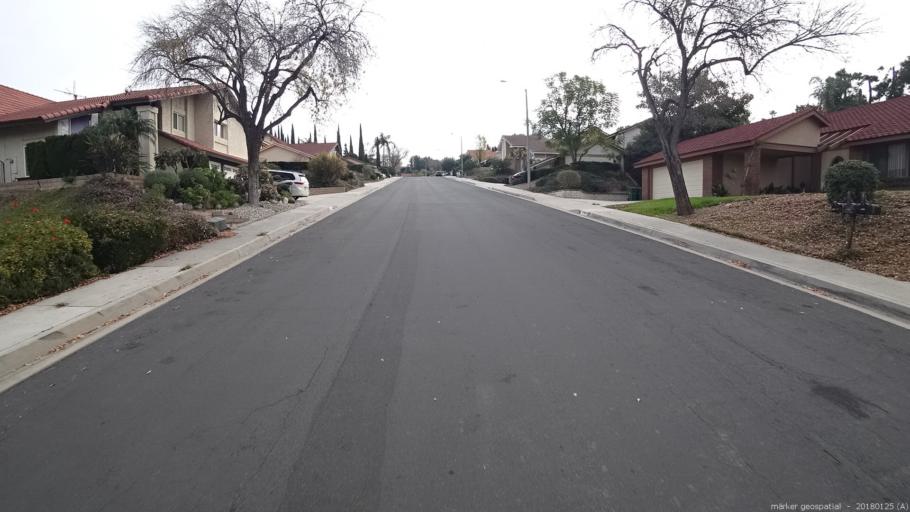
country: US
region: California
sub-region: Los Angeles County
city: Walnut
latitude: 33.9659
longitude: -117.8403
